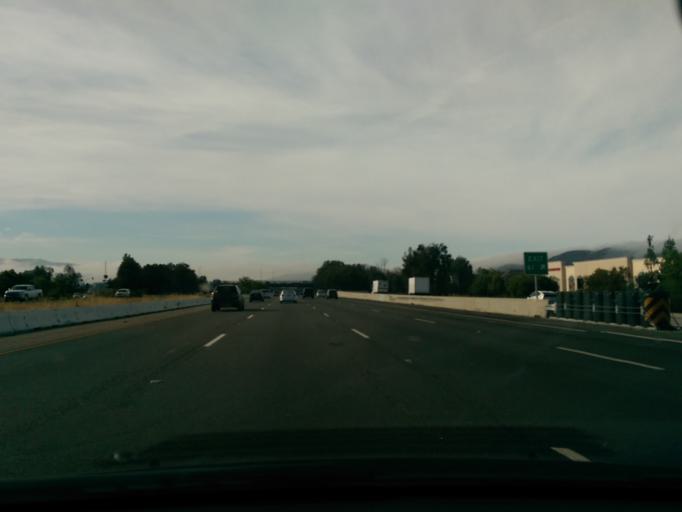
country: US
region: California
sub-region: Riverside County
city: Murrieta Hot Springs
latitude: 33.5262
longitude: -117.1656
